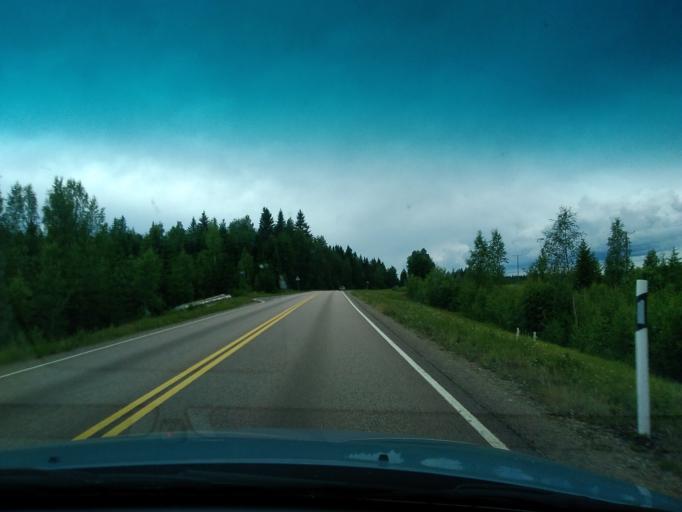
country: FI
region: Central Finland
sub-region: Keuruu
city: Multia
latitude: 62.3905
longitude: 24.7657
